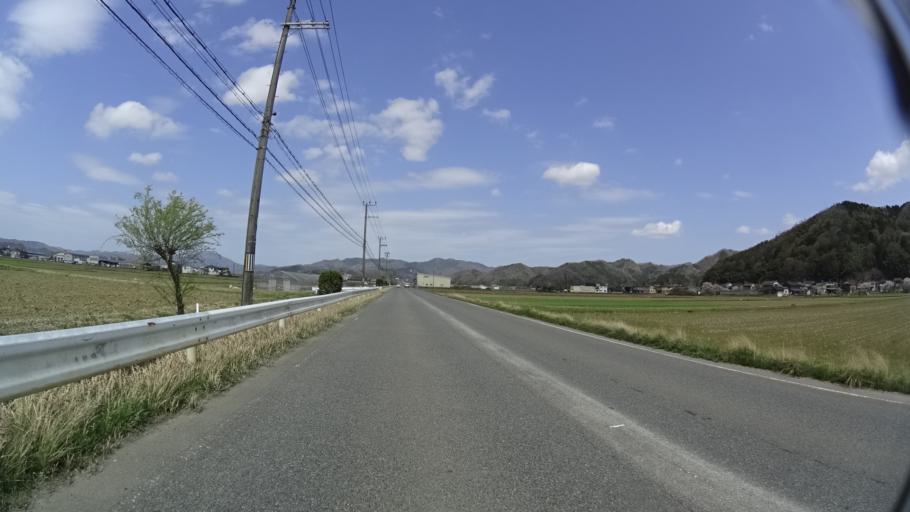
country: JP
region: Hyogo
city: Toyooka
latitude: 35.5209
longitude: 134.8399
